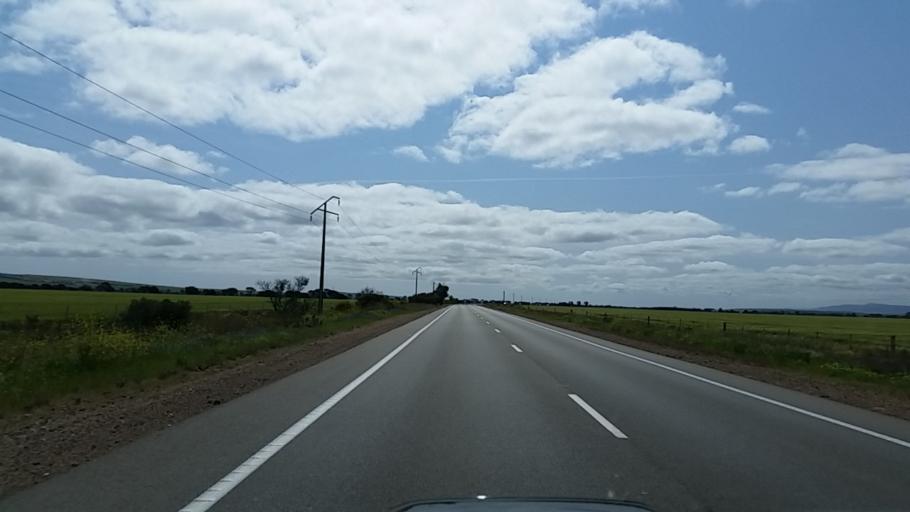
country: AU
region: South Australia
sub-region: Port Pirie City and Dists
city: Crystal Brook
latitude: -33.4759
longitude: 138.1683
